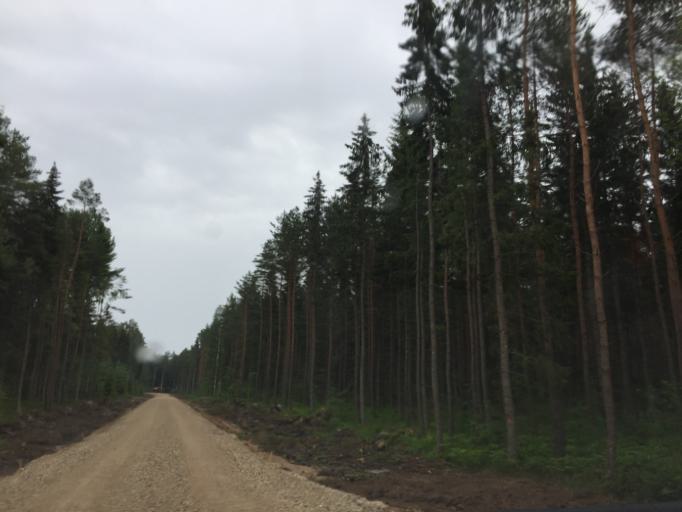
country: LV
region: Tukuma Rajons
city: Tukums
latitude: 57.0051
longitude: 23.1047
